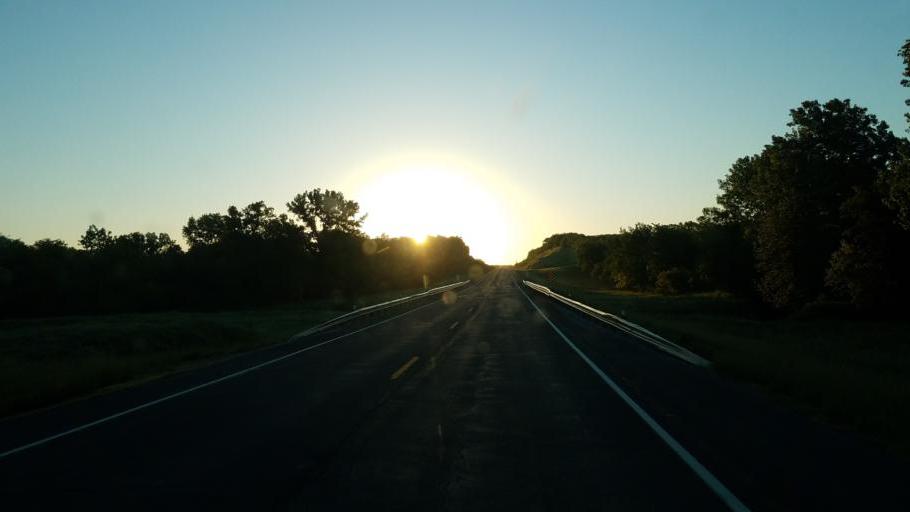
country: US
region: Missouri
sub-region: Schuyler County
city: Lancaster
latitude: 40.4880
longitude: -92.6234
